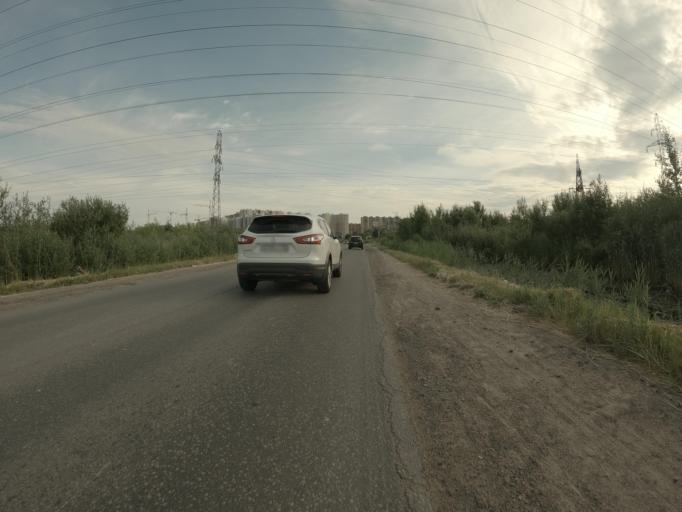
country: RU
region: St.-Petersburg
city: Krasnogvargeisky
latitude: 59.9254
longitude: 30.5191
